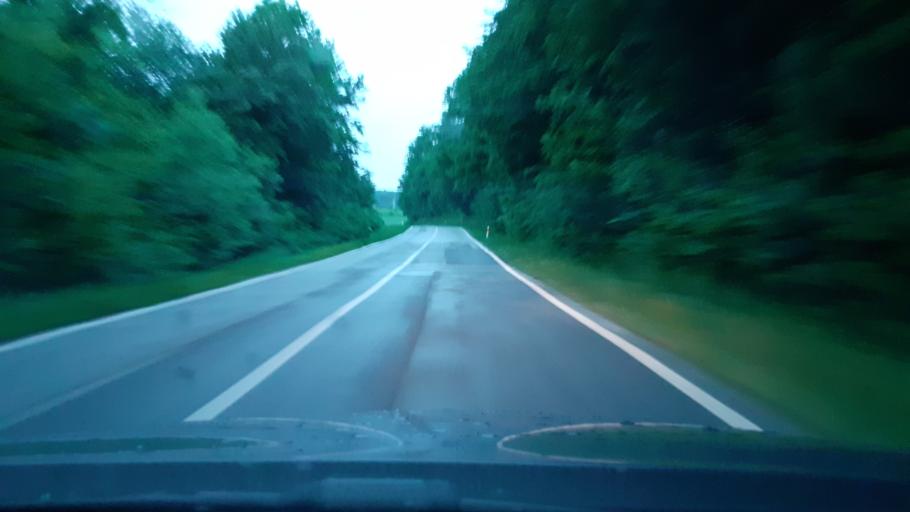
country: HR
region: Pozesko-Slavonska
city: Bilice
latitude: 45.1931
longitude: 17.8487
